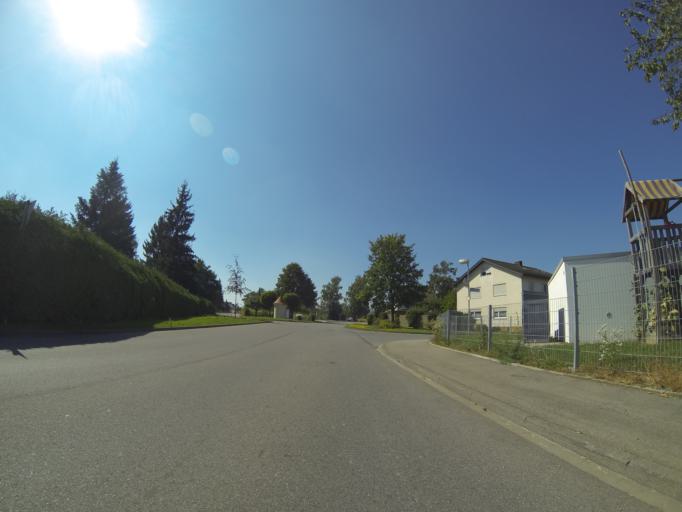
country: DE
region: Baden-Wuerttemberg
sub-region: Tuebingen Region
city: Erbach
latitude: 48.3063
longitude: 9.9078
